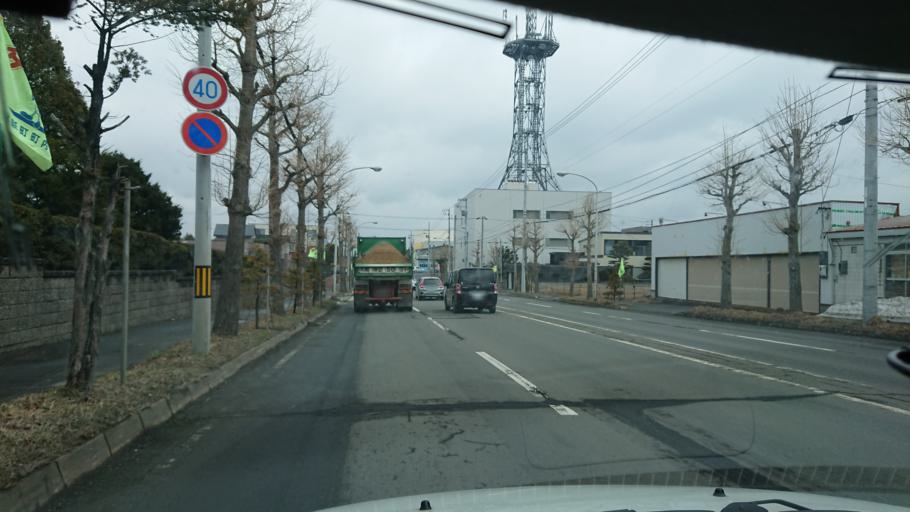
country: JP
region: Hokkaido
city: Kitahiroshima
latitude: 42.8816
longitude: 141.5734
